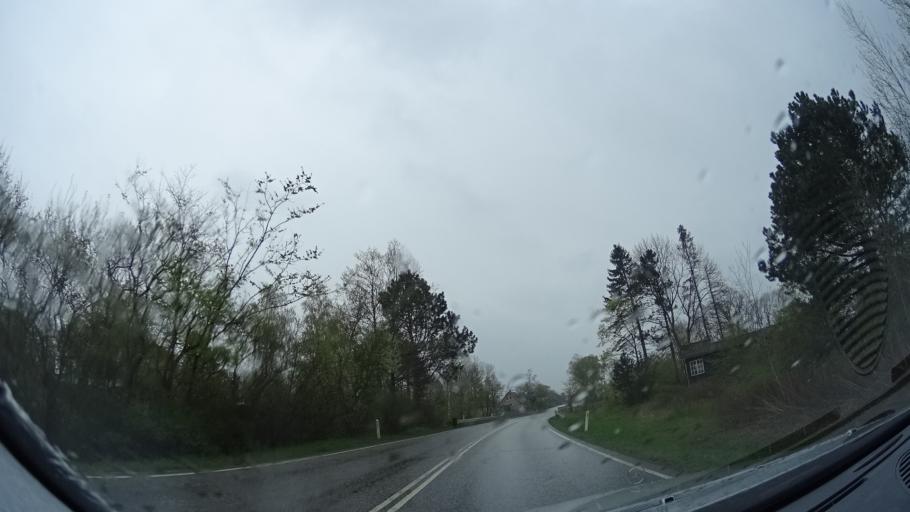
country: DK
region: Zealand
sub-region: Holbaek Kommune
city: Holbaek
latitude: 55.7725
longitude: 11.6269
